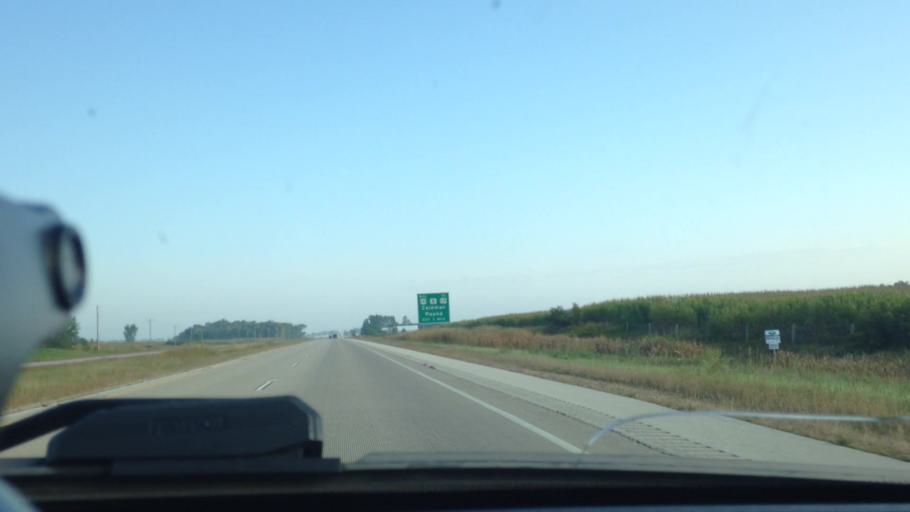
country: US
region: Wisconsin
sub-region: Oconto County
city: Oconto Falls
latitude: 45.0393
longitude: -88.0444
